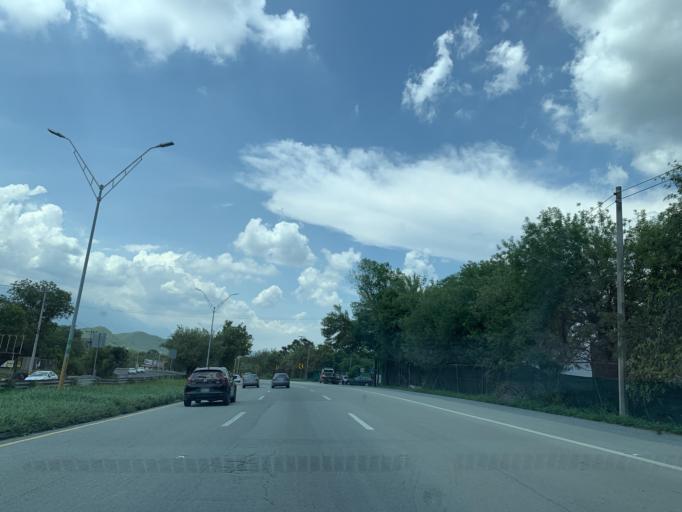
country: MX
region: Nuevo Leon
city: Santiago
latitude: 25.3947
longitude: -100.1217
